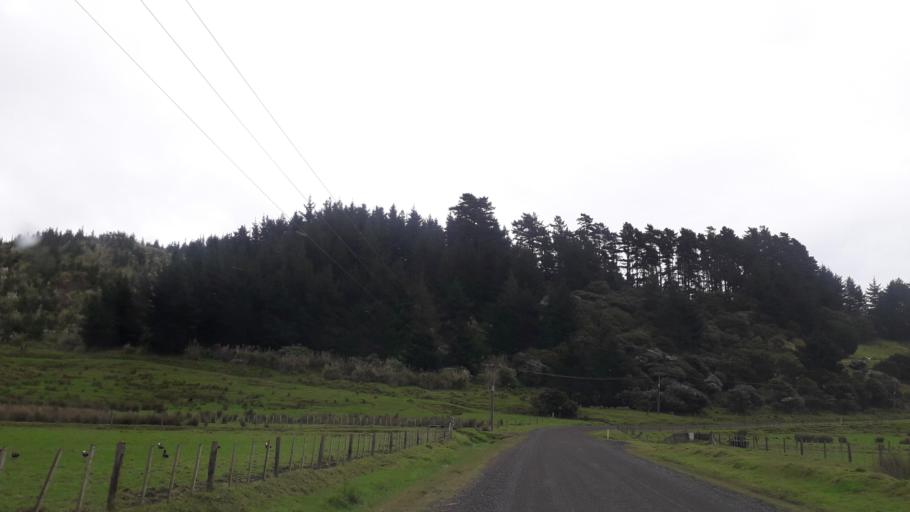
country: NZ
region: Northland
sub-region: Far North District
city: Ahipara
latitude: -35.4403
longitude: 173.3263
